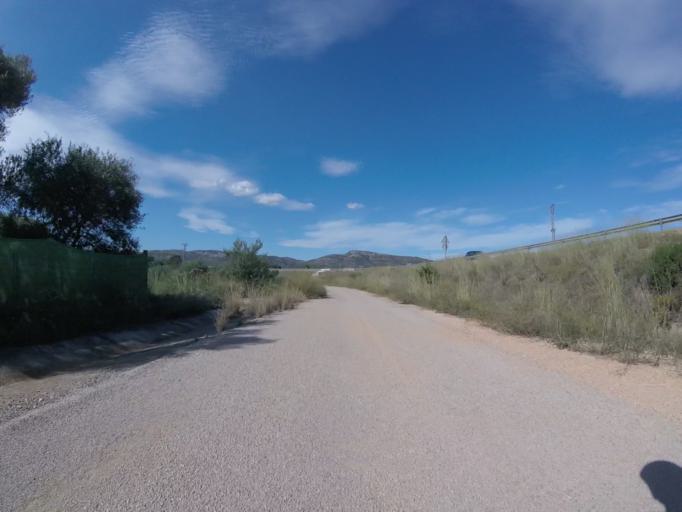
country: ES
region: Valencia
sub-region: Provincia de Castello
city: Peniscola
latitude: 40.3956
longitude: 0.3659
